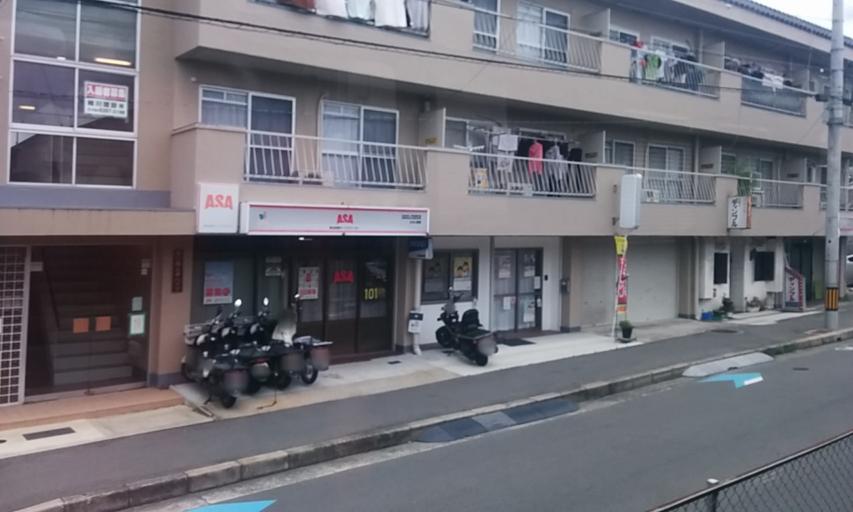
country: JP
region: Osaka
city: Mino
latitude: 34.8296
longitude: 135.4670
